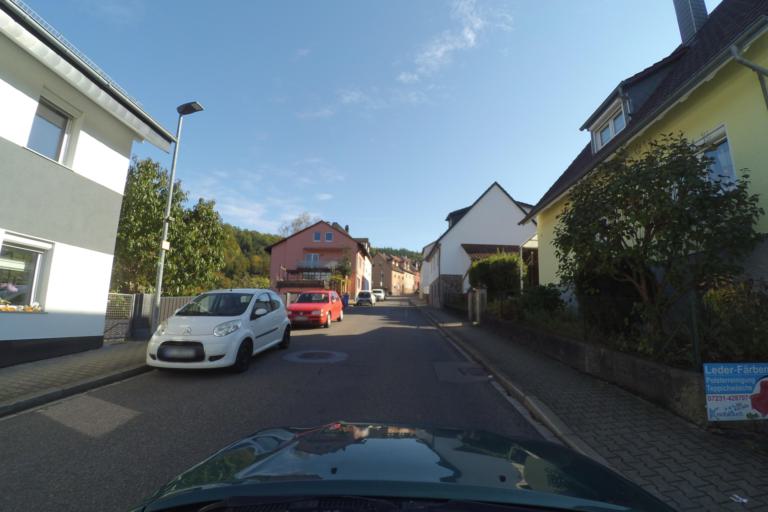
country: DE
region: Baden-Wuerttemberg
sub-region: Karlsruhe Region
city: Unterreichenbach
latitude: 48.8606
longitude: 8.7389
